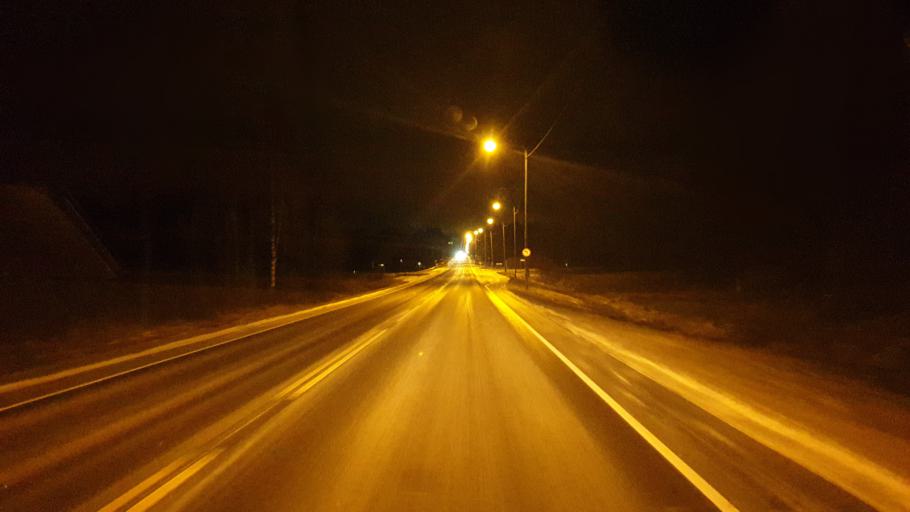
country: FI
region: Central Finland
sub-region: AEaenekoski
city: AEaenekoski
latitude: 62.4898
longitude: 25.6784
